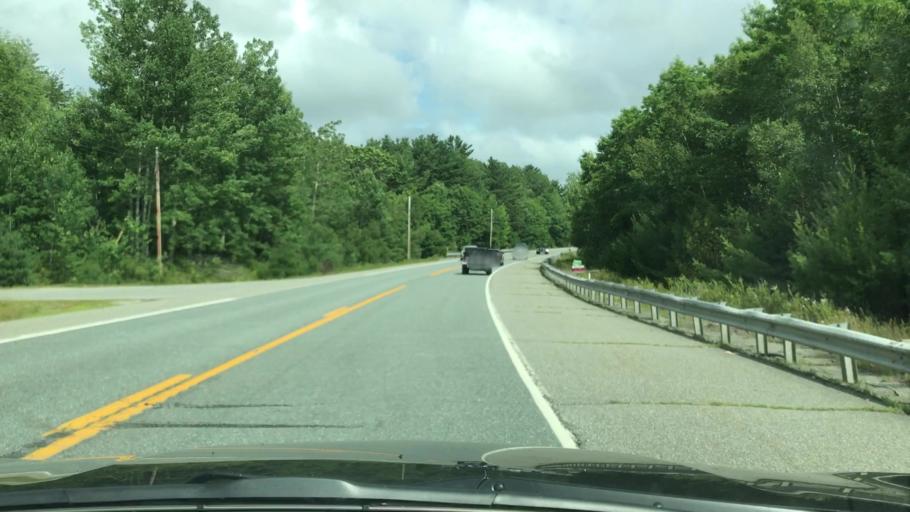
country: US
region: Maine
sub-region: Hancock County
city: Surry
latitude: 44.5635
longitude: -68.5907
